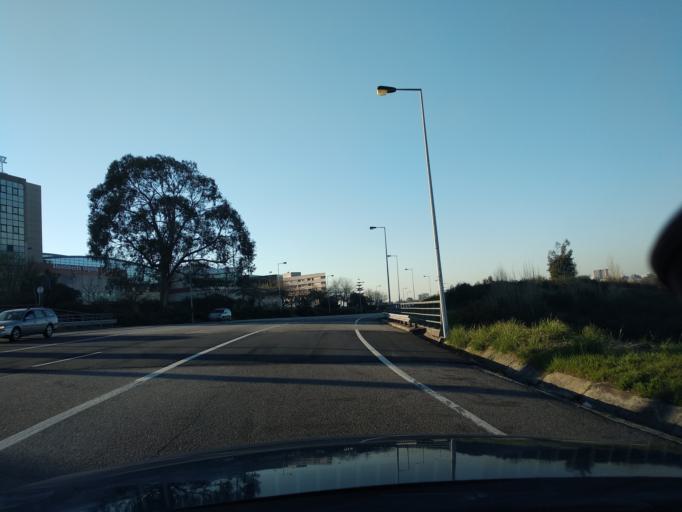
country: PT
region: Porto
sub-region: Vila Nova de Gaia
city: Vila Nova de Gaia
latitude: 41.1407
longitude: -8.6339
